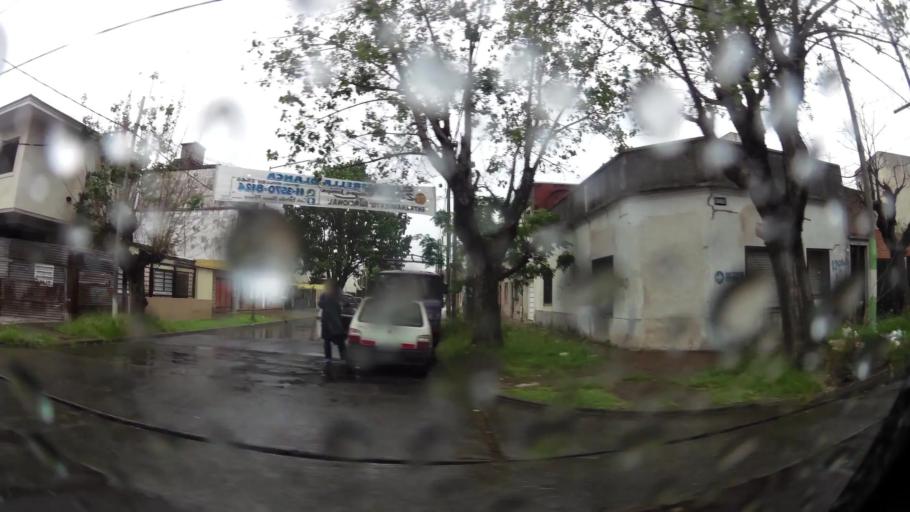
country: AR
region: Buenos Aires
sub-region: Partido de Lanus
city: Lanus
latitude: -34.7027
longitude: -58.4101
